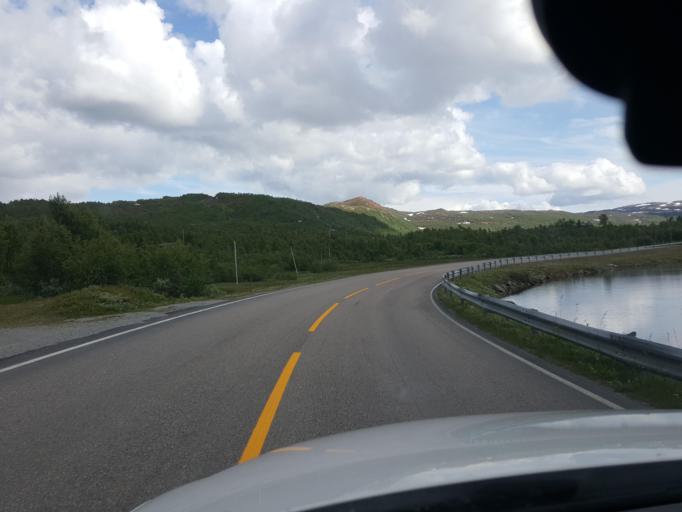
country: NO
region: Nordland
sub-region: Rana
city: Mo i Rana
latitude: 66.2901
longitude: 14.4971
